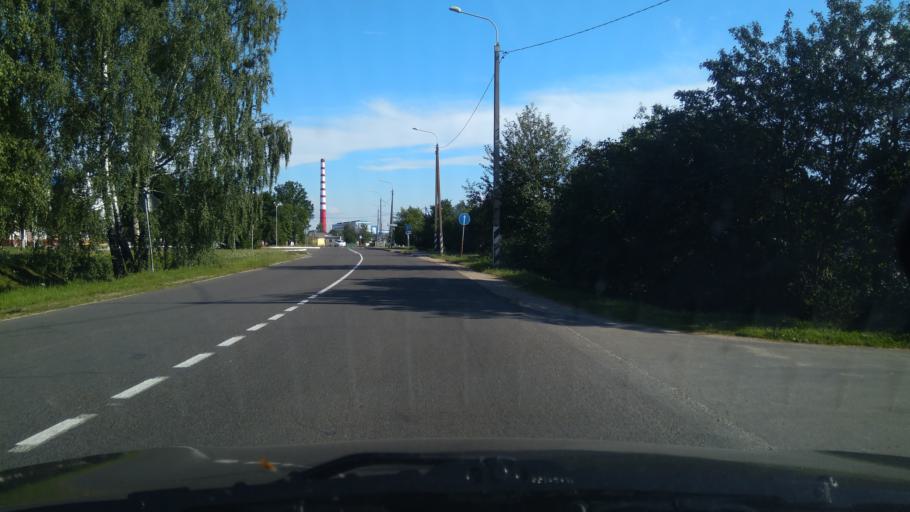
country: BY
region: Brest
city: Byelaazyorsk
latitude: 52.4674
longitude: 25.1856
